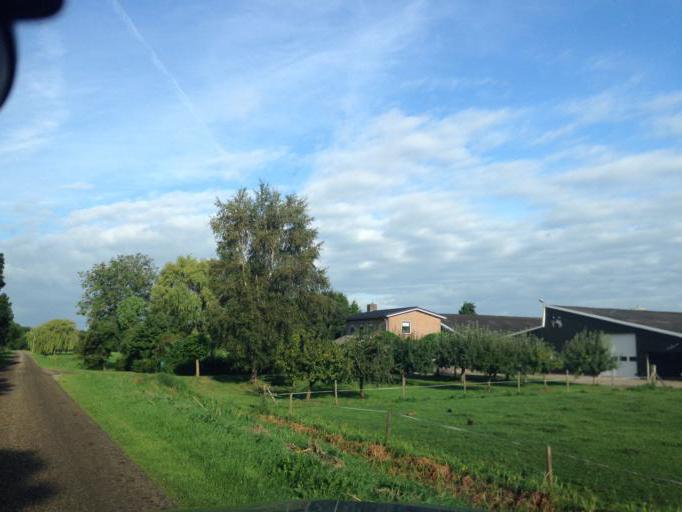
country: NL
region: South Holland
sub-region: Gemeente Leerdam
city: Leerdam
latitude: 51.8615
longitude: 5.1728
